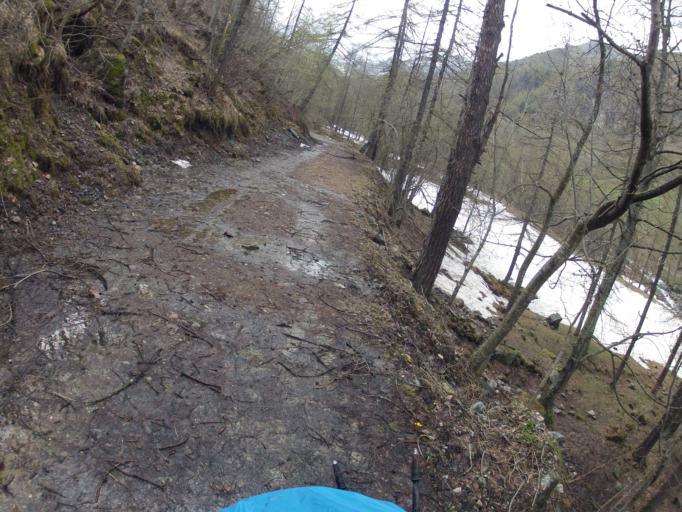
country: IT
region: Piedmont
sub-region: Provincia di Cuneo
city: Crissolo
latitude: 44.7011
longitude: 7.1389
